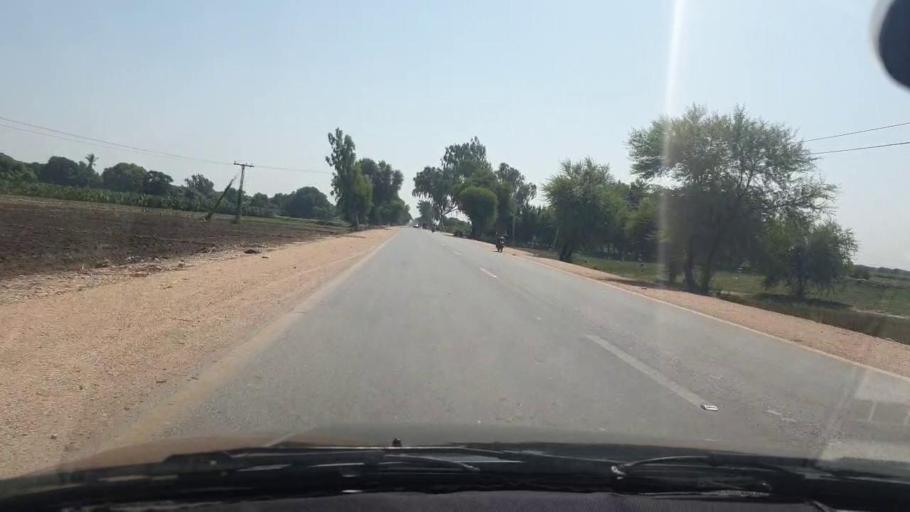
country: PK
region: Sindh
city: Tando Allahyar
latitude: 25.4408
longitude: 68.7368
